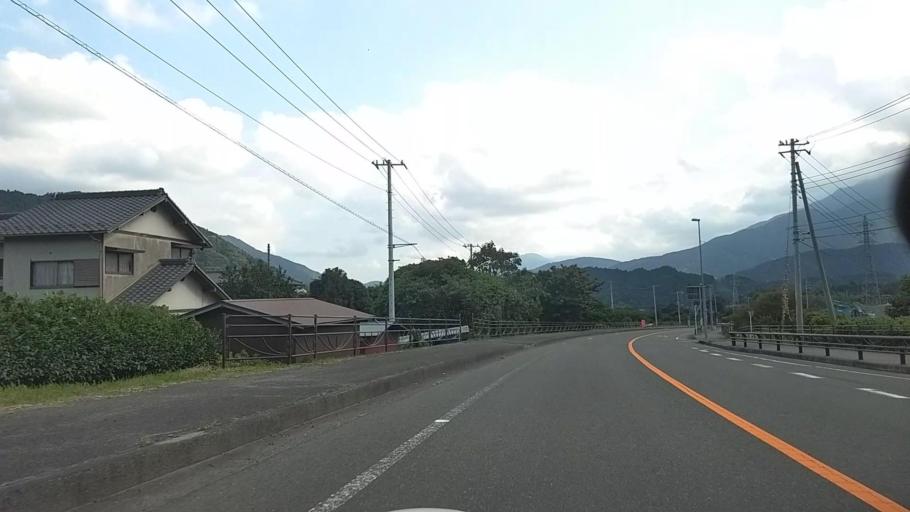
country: JP
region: Shizuoka
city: Fujinomiya
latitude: 35.3081
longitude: 138.4476
